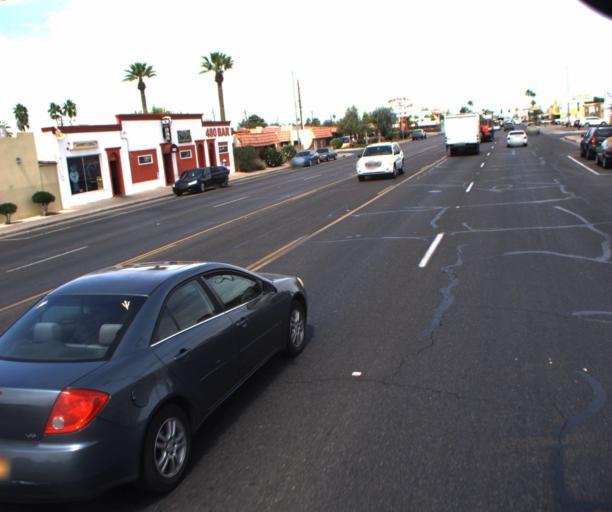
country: US
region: Arizona
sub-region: Maricopa County
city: Chandler
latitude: 33.3108
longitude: -111.8414
